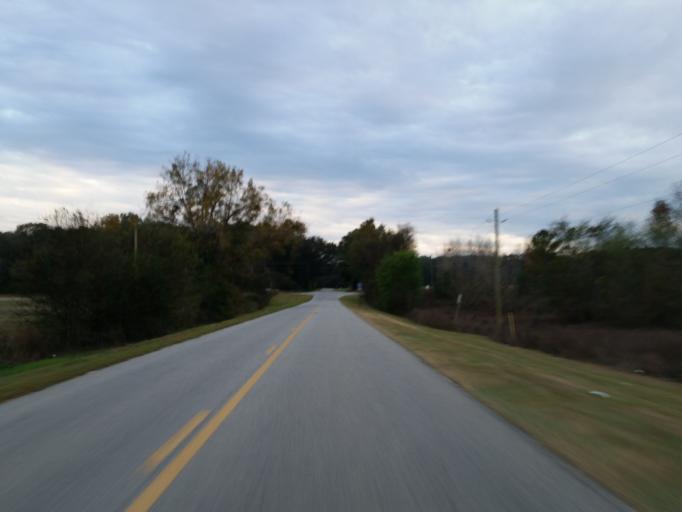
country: US
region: Florida
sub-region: Hamilton County
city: Jasper
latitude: 30.5289
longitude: -83.1026
